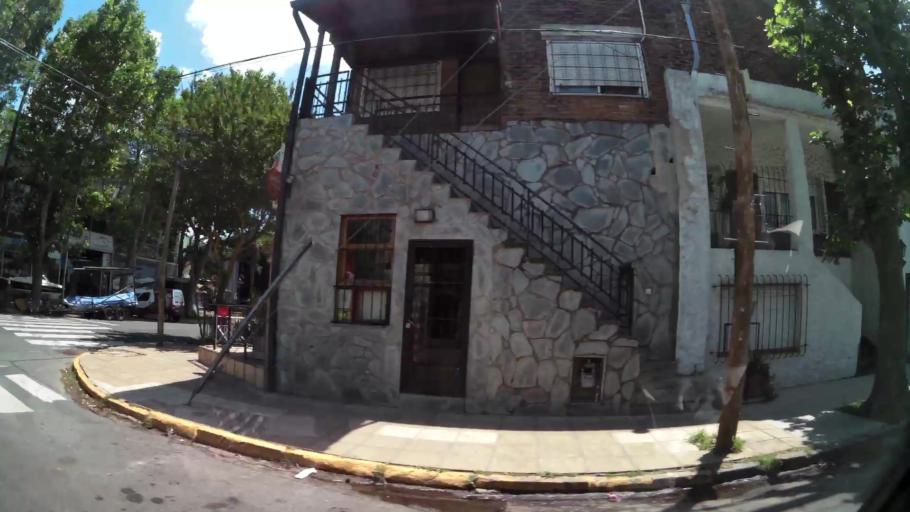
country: AR
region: Buenos Aires
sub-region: Partido de Tigre
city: Tigre
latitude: -34.4107
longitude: -58.5926
